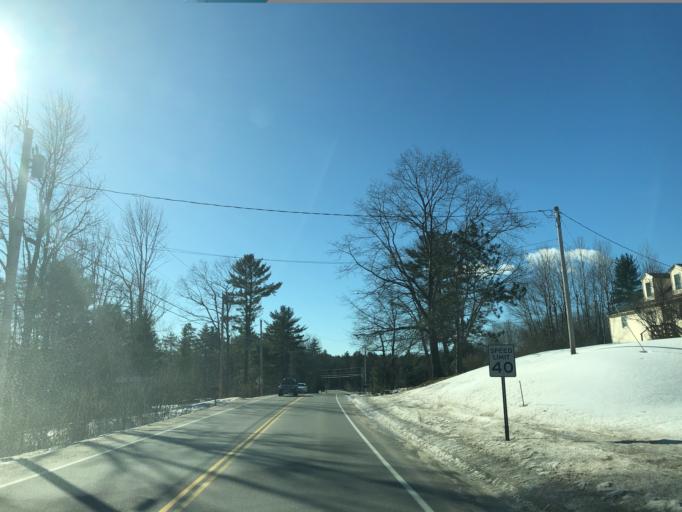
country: US
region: Maine
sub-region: Cumberland County
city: South Windham
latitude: 43.7661
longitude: -70.4396
